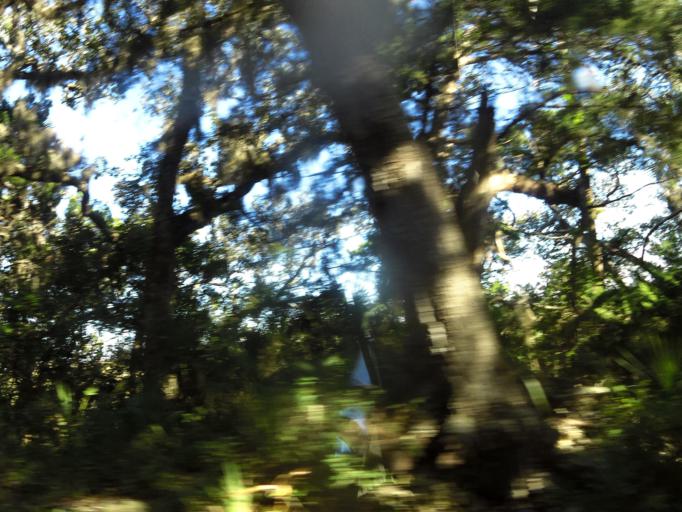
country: US
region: Florida
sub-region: Duval County
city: Atlantic Beach
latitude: 30.4161
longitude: -81.4278
